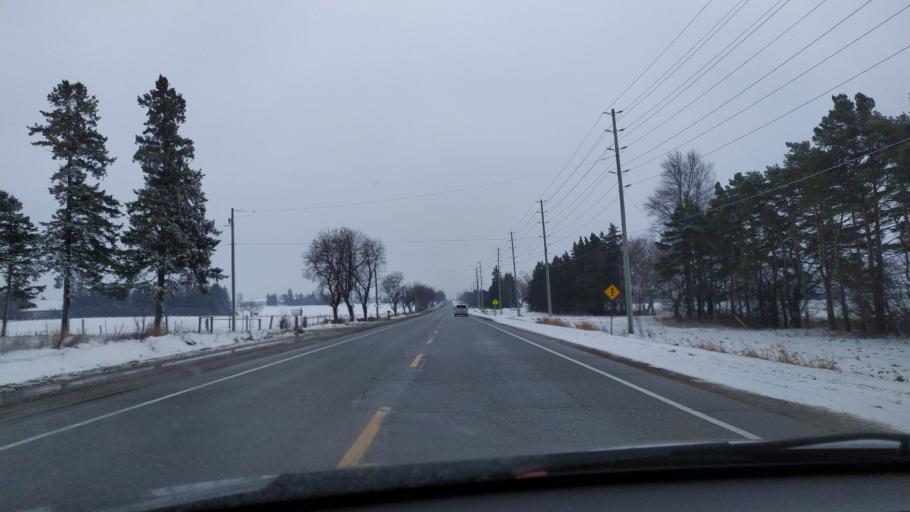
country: CA
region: Ontario
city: Waterloo
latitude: 43.6169
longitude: -80.6776
